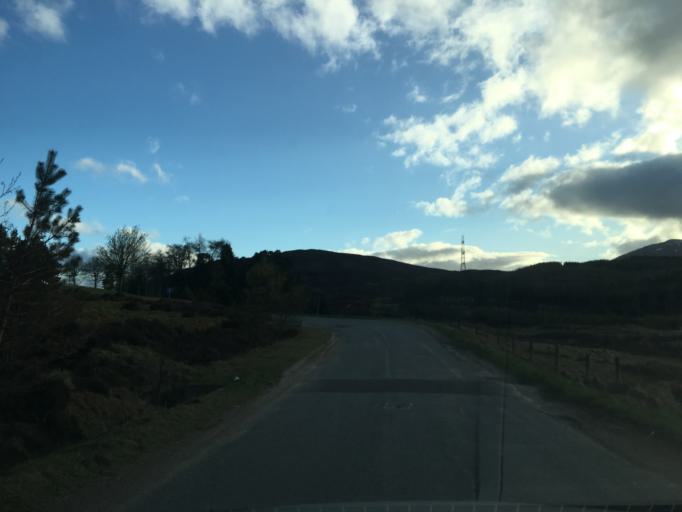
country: GB
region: Scotland
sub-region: Perth and Kinross
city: Aberfeldy
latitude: 56.6672
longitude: -3.9951
